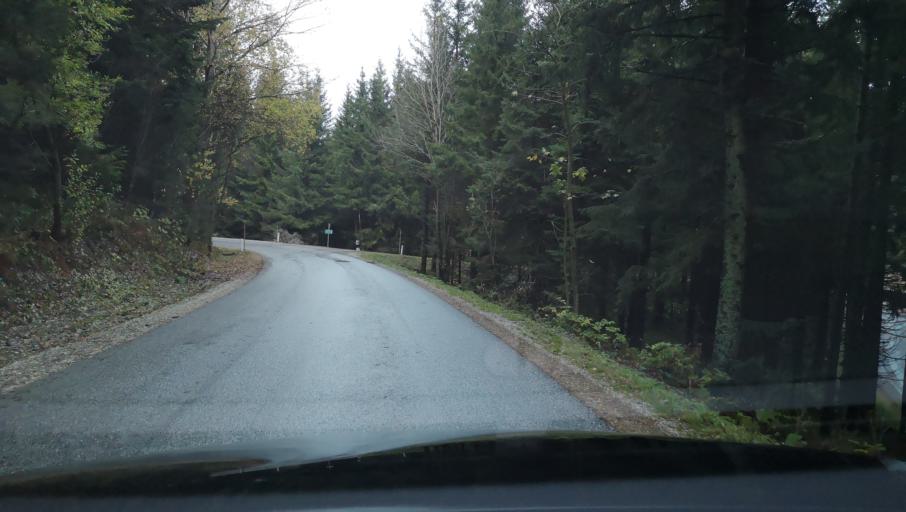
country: AT
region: Styria
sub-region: Politischer Bezirk Weiz
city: Gasen
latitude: 47.3576
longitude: 15.5891
